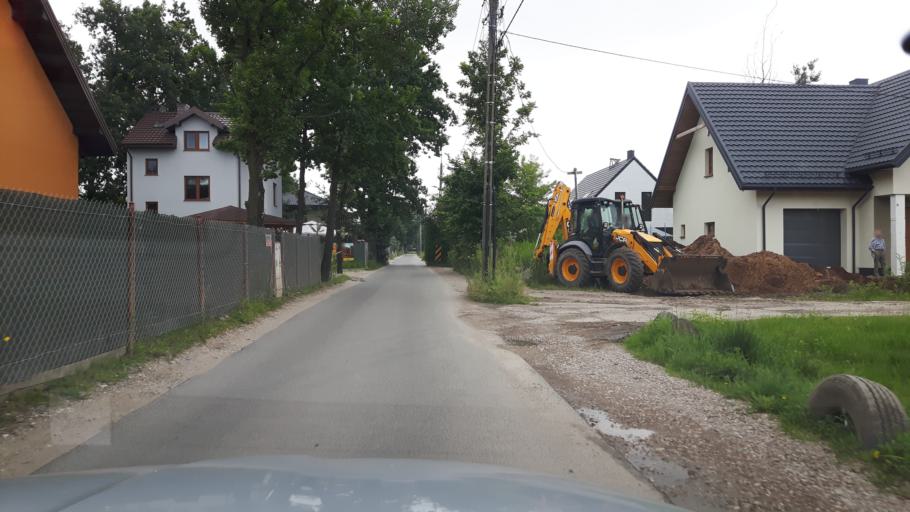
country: PL
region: Masovian Voivodeship
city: Zielonka
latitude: 52.2880
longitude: 21.1687
